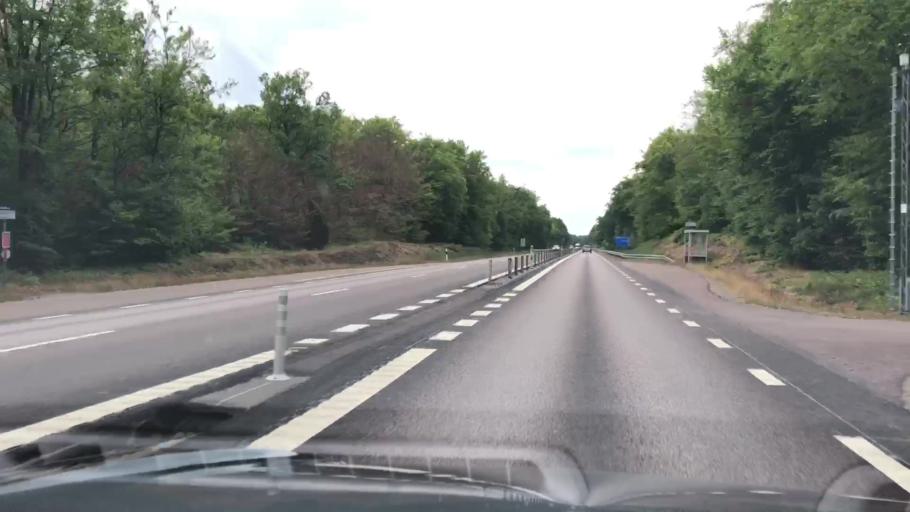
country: SE
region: Blekinge
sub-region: Karlskrona Kommun
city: Jaemjoe
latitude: 56.2364
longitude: 15.9228
